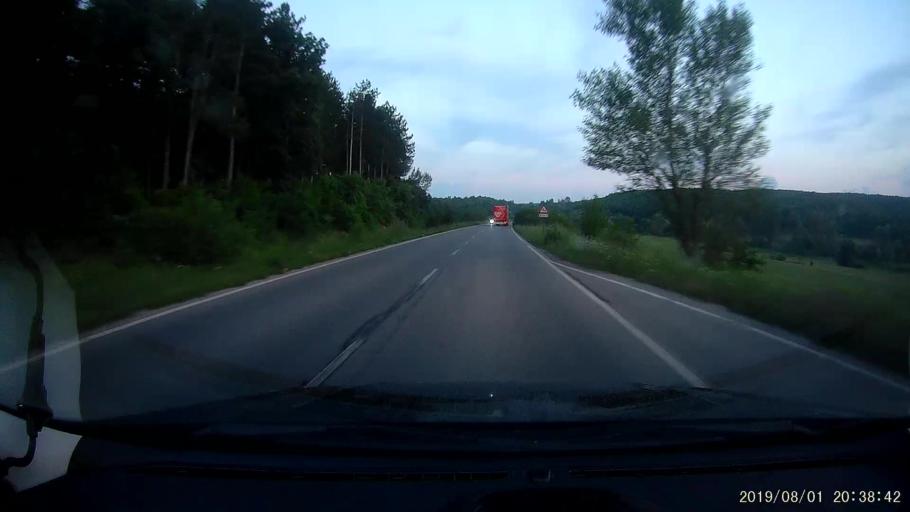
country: BG
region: Yambol
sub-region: Obshtina Elkhovo
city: Elkhovo
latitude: 42.0203
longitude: 26.6017
